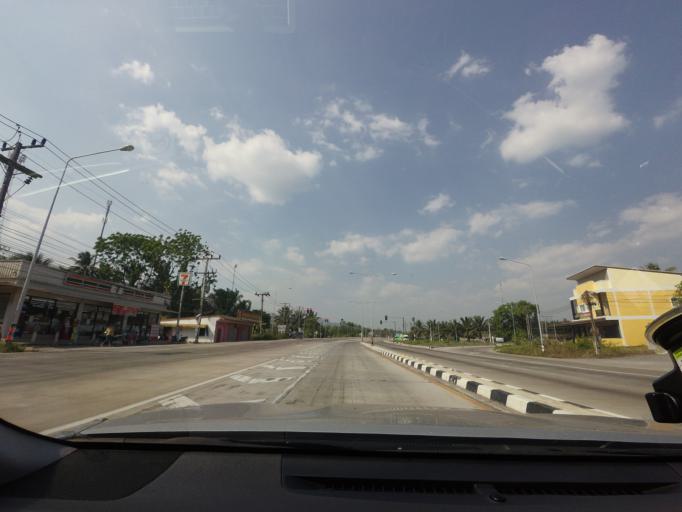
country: TH
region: Phangnga
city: Thap Put
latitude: 8.5770
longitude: 98.7407
